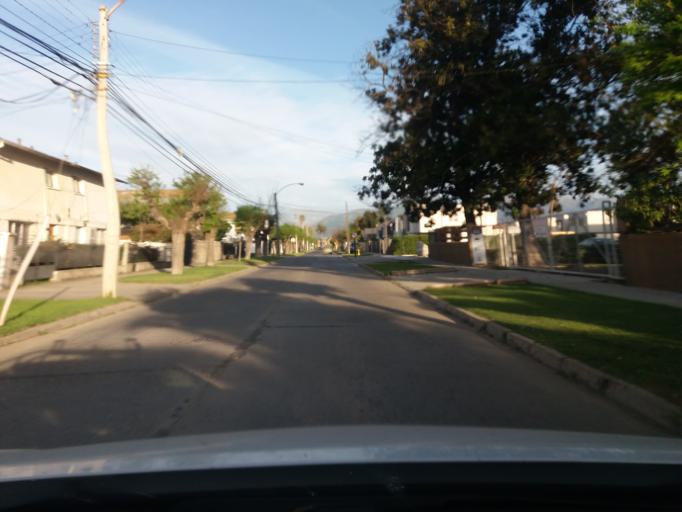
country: CL
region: Valparaiso
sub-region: Provincia de Marga Marga
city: Limache
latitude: -32.9915
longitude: -71.2684
